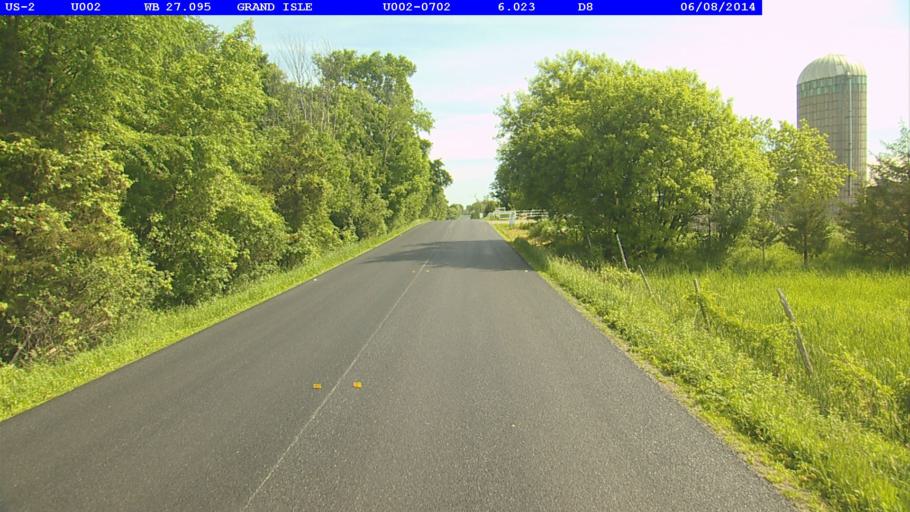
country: US
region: New York
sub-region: Clinton County
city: Cumberland Head
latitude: 44.6834
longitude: -73.3136
